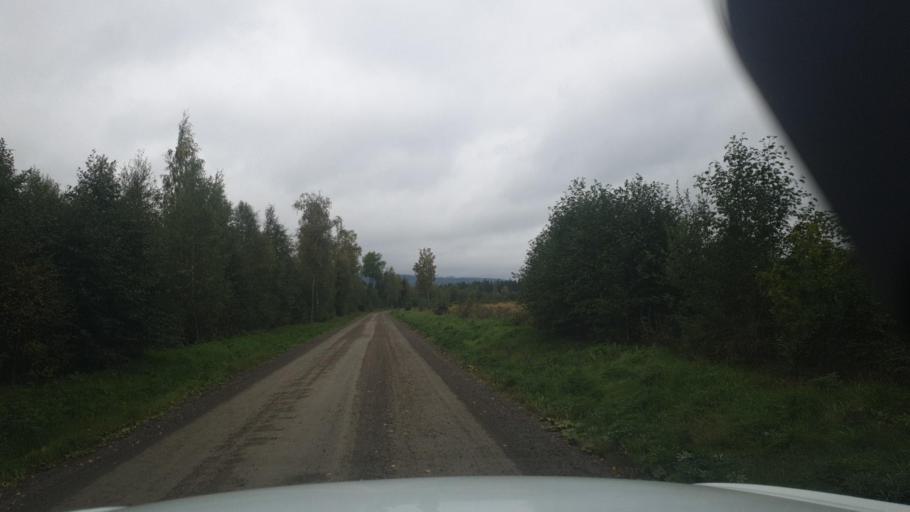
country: SE
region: Vaermland
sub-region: Sunne Kommun
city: Sunne
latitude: 59.8035
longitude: 13.0905
